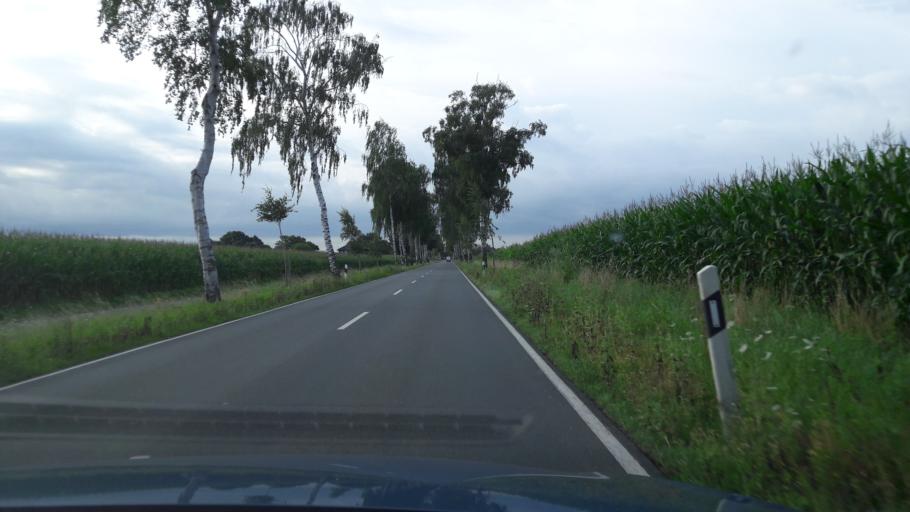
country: DE
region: North Rhine-Westphalia
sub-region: Regierungsbezirk Munster
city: Everswinkel
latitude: 51.8797
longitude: 7.8967
